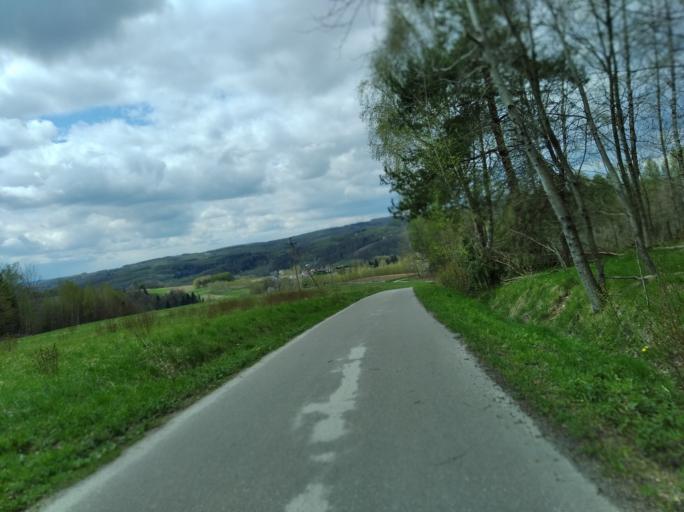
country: PL
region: Subcarpathian Voivodeship
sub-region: Powiat strzyzowski
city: Niebylec
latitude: 49.8826
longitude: 21.9235
